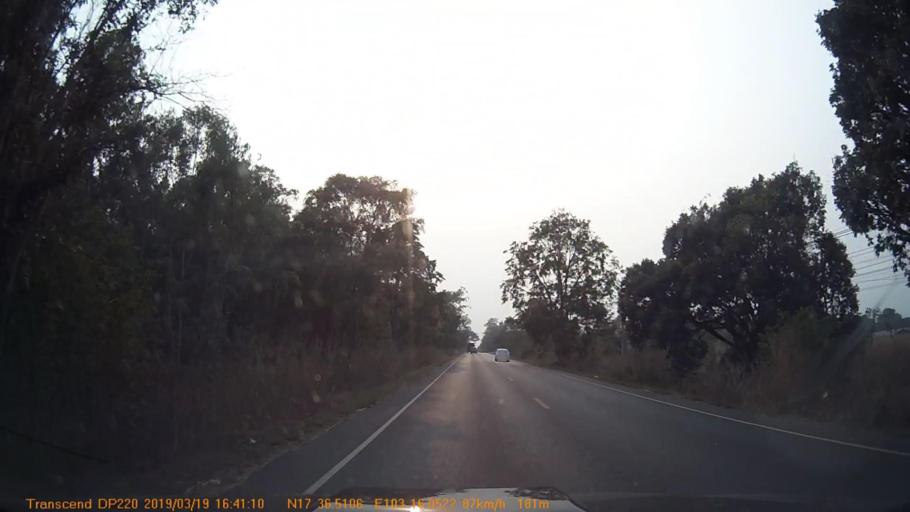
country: TH
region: Changwat Udon Thani
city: Ban Dung
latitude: 17.6085
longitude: 103.2669
